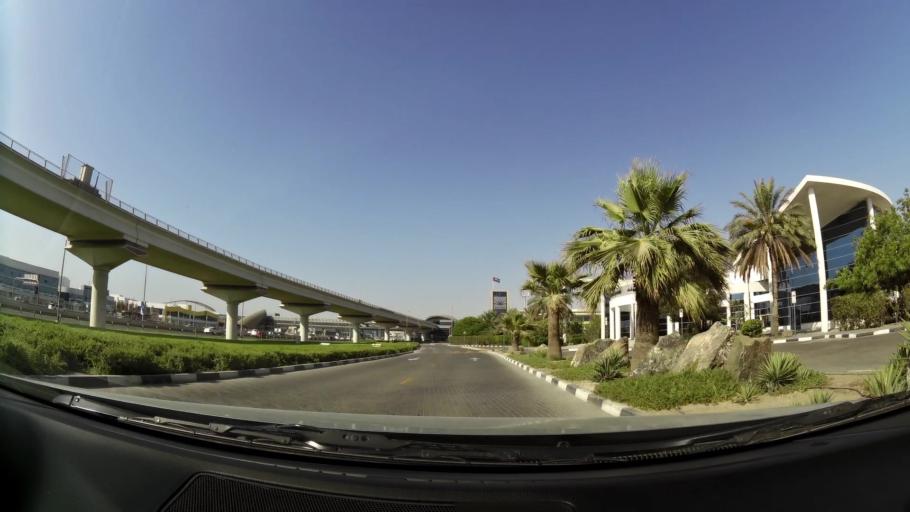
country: AE
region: Dubai
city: Dubai
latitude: 25.1246
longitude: 55.2055
